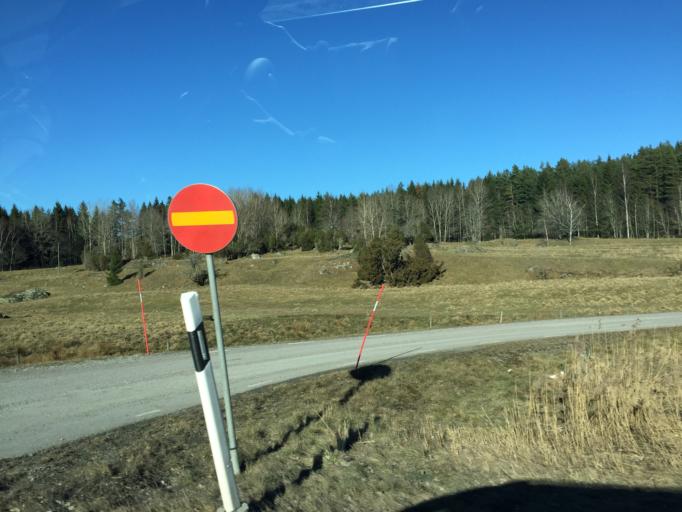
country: SE
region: OEstergoetland
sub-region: Finspangs Kommun
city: Finspang
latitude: 58.7120
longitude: 15.7149
